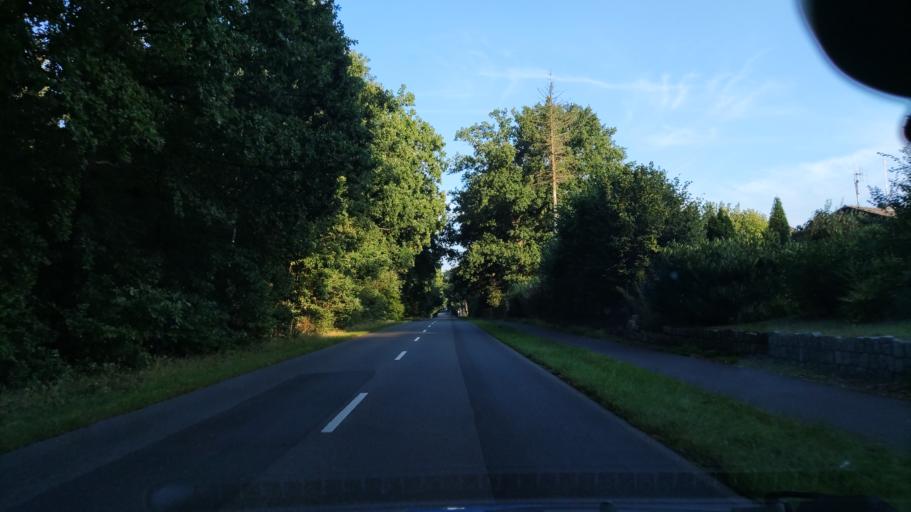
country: DE
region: Lower Saxony
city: Fassberg
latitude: 52.9641
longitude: 10.1762
